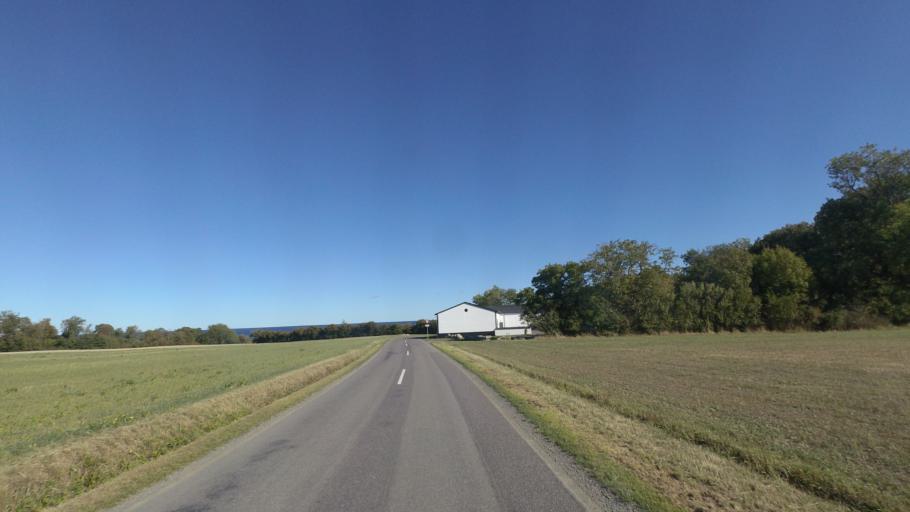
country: DK
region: Capital Region
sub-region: Bornholm Kommune
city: Nexo
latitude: 55.1102
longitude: 15.1368
